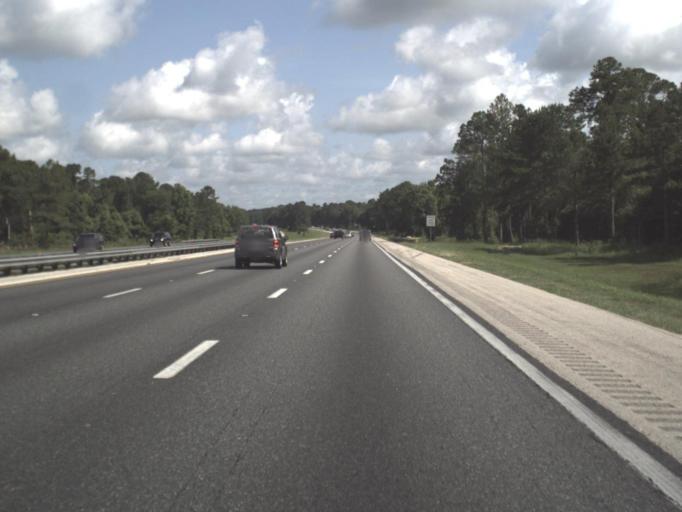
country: US
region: Florida
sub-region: Alachua County
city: Gainesville
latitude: 29.5047
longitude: -82.2981
